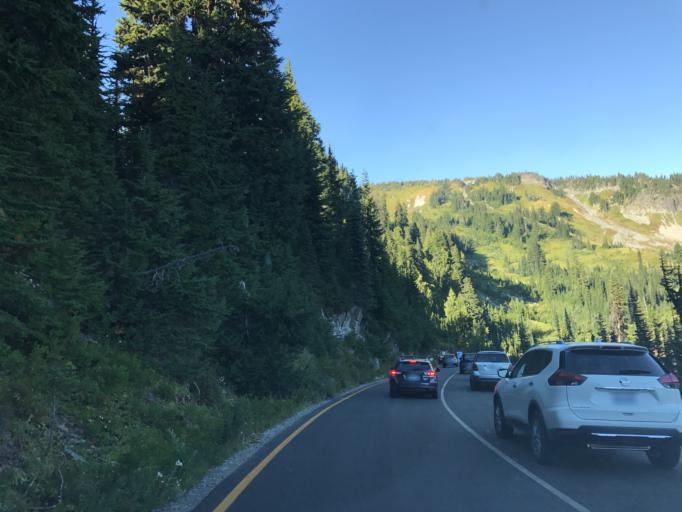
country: US
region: Washington
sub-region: Pierce County
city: Buckley
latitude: 46.7893
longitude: -121.7312
